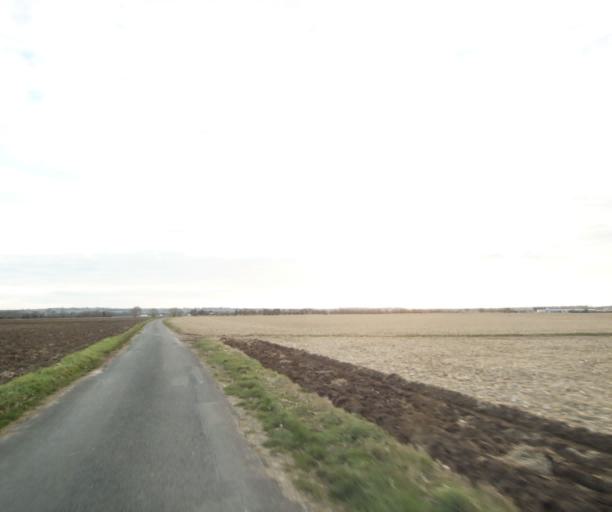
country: FR
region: Poitou-Charentes
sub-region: Departement de la Charente-Maritime
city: Les Gonds
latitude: 45.7070
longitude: -0.6133
